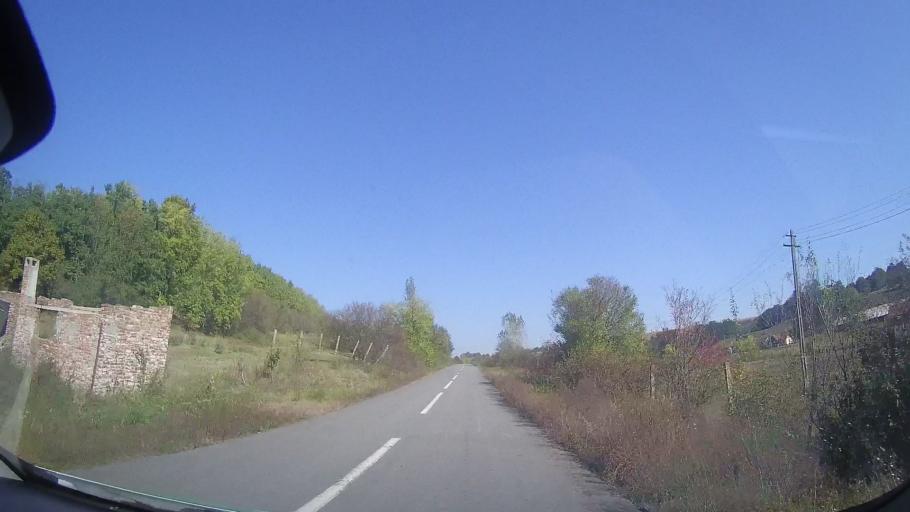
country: RO
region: Timis
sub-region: Comuna Bara
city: Bara
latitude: 45.8712
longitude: 21.8825
